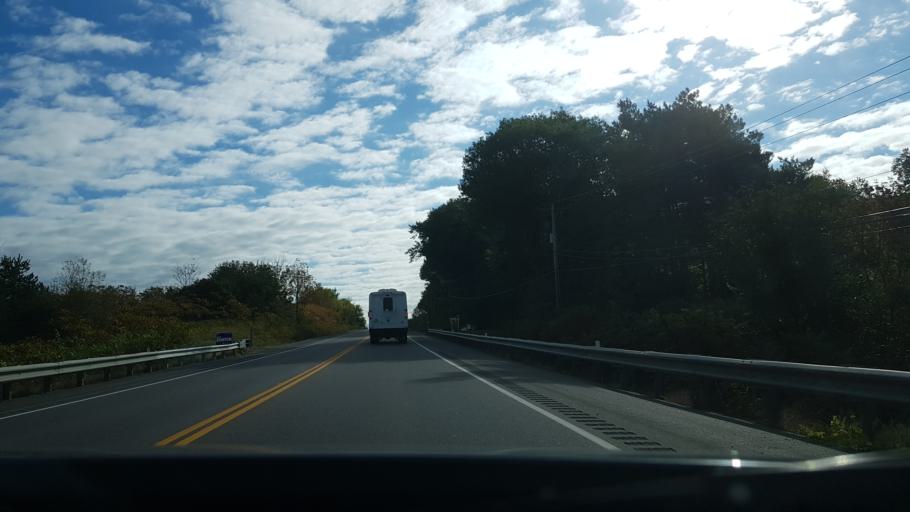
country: CA
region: Ontario
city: Orillia
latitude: 44.6138
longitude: -79.4818
